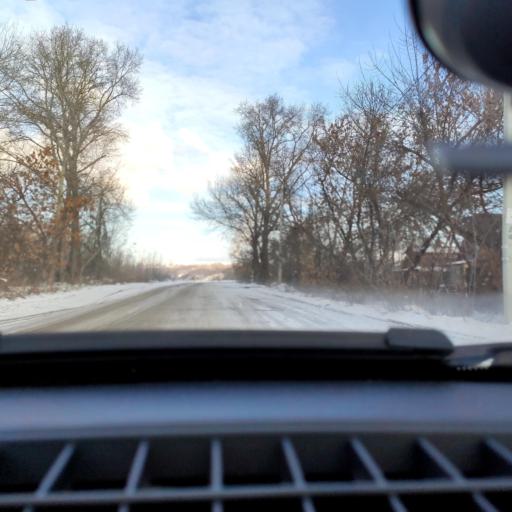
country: RU
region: Bashkortostan
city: Ufa
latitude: 54.8315
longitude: 56.0579
